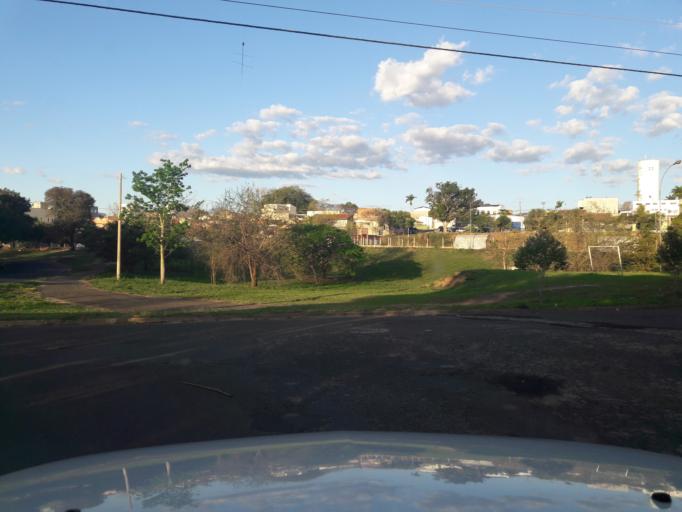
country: BR
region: Sao Paulo
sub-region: Moji-Guacu
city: Mogi-Gaucu
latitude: -22.3935
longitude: -46.9489
